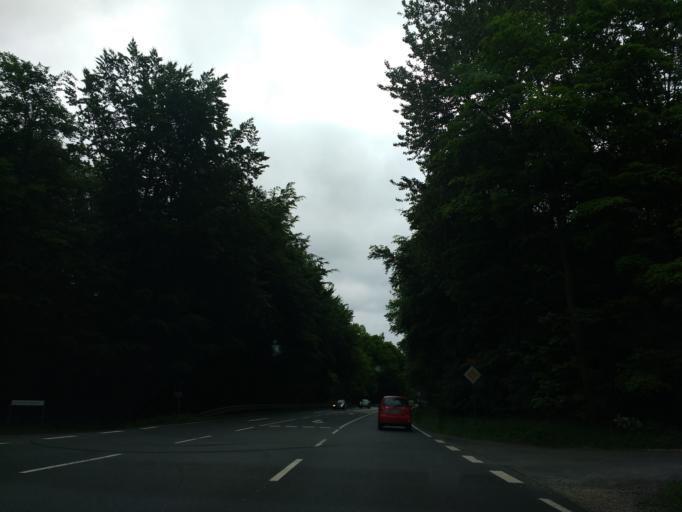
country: DE
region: Lower Saxony
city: Gross Munzel
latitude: 52.4131
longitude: 9.5059
